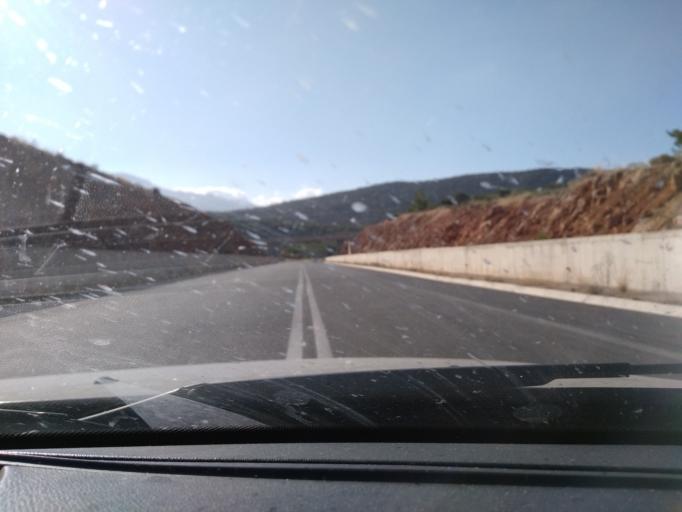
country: GR
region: Crete
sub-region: Nomos Lasithiou
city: Agios Nikolaos
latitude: 35.1387
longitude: 25.7110
